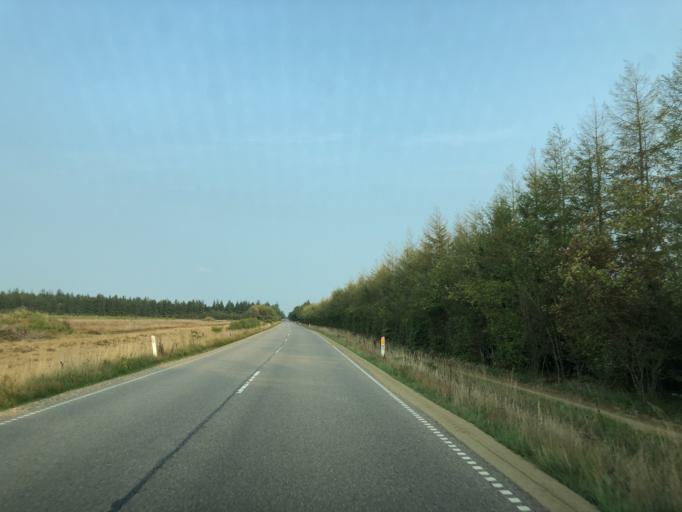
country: DK
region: South Denmark
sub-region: Billund Kommune
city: Grindsted
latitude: 55.8306
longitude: 8.9576
